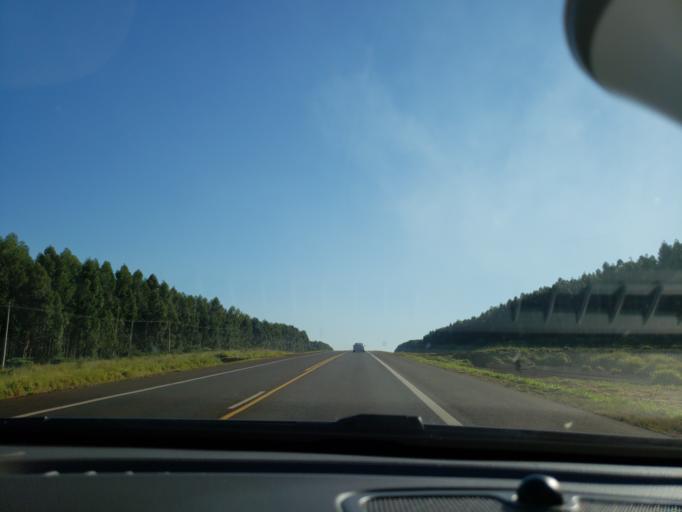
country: AR
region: Misiones
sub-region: Departamento de Capital
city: Posadas
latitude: -27.4653
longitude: -55.9427
